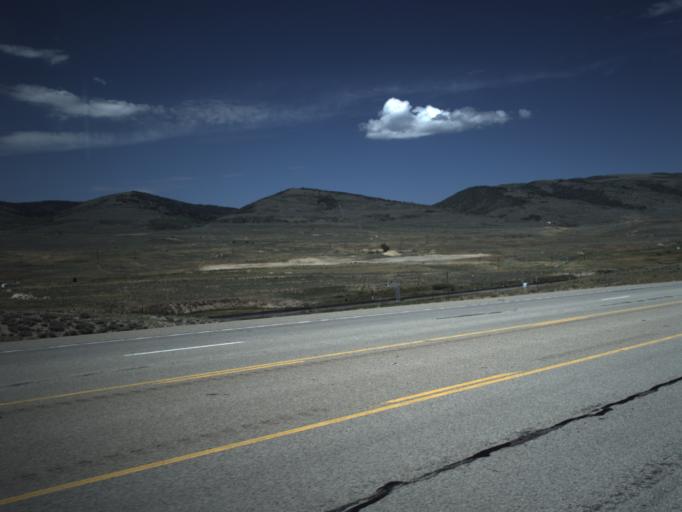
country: US
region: Utah
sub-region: Carbon County
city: Helper
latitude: 39.8480
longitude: -111.0065
